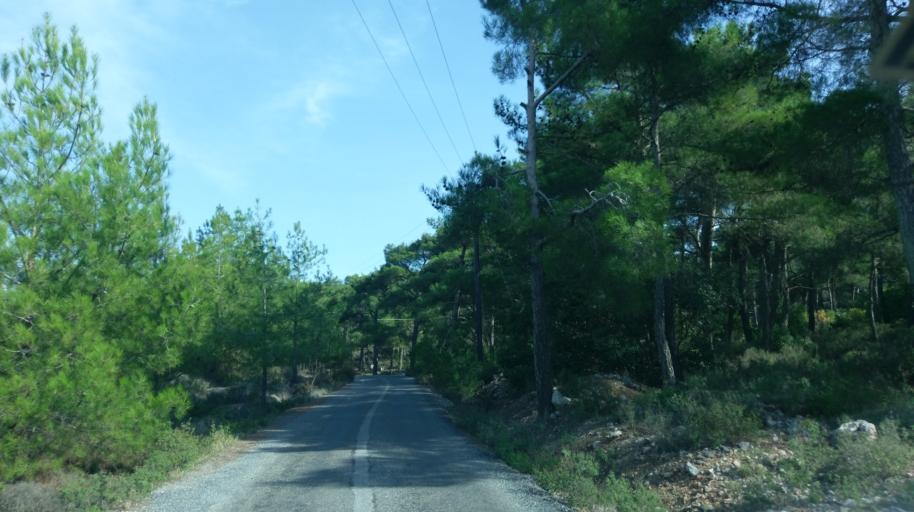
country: CY
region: Keryneia
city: Kyrenia
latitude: 35.3069
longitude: 33.2459
